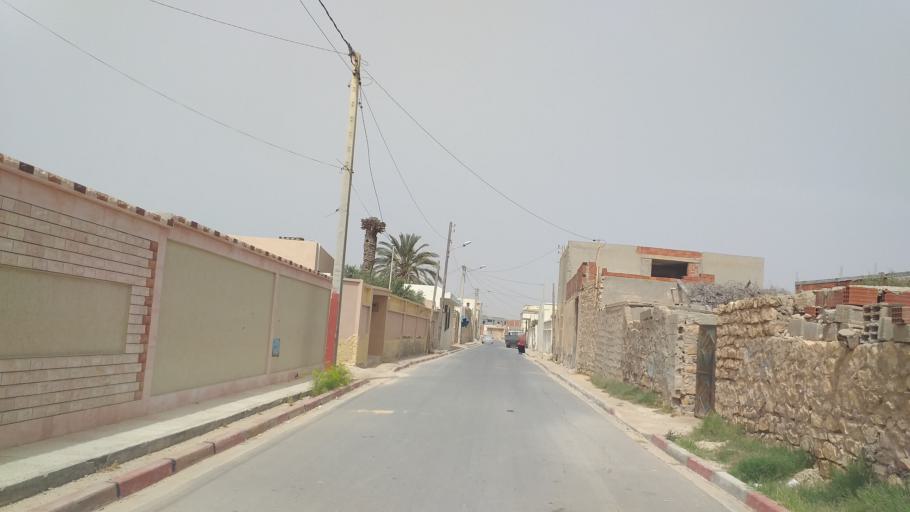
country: TN
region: Qabis
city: Gabes
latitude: 33.9410
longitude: 10.0600
